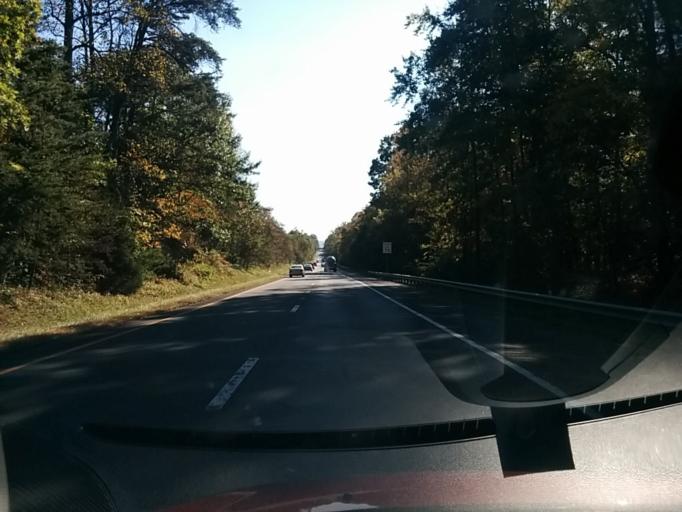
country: US
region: Virginia
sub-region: Albemarle County
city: Crozet
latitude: 38.0403
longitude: -78.7154
